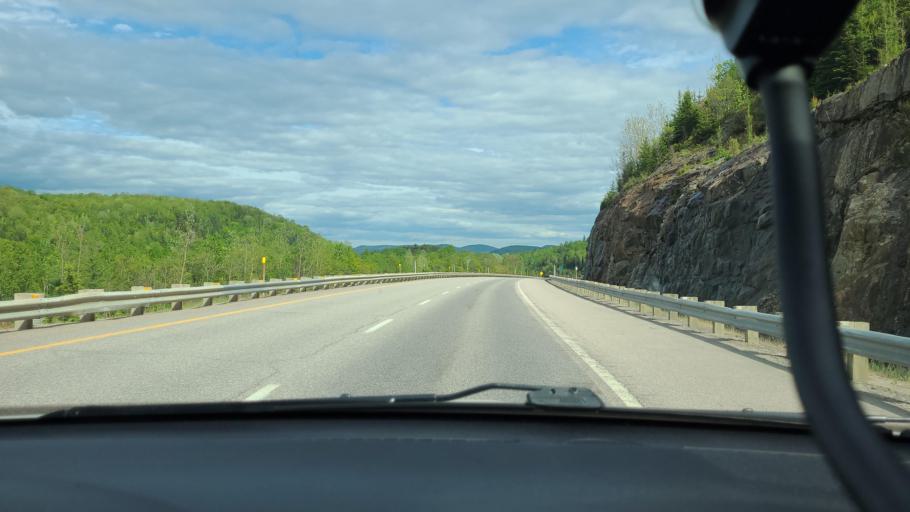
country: CA
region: Quebec
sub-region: Laurentides
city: Mont-Tremblant
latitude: 46.1385
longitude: -74.6350
